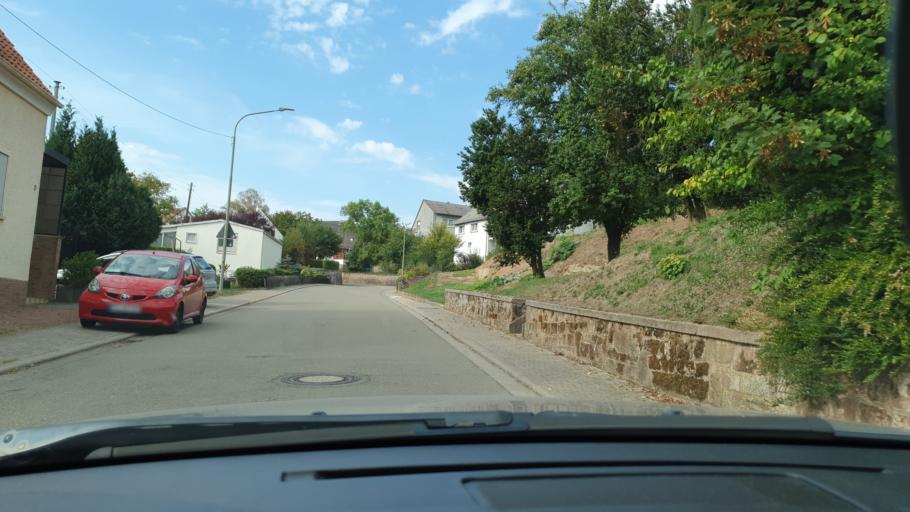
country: DE
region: Rheinland-Pfalz
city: Grossbundenbach
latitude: 49.3053
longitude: 7.4223
